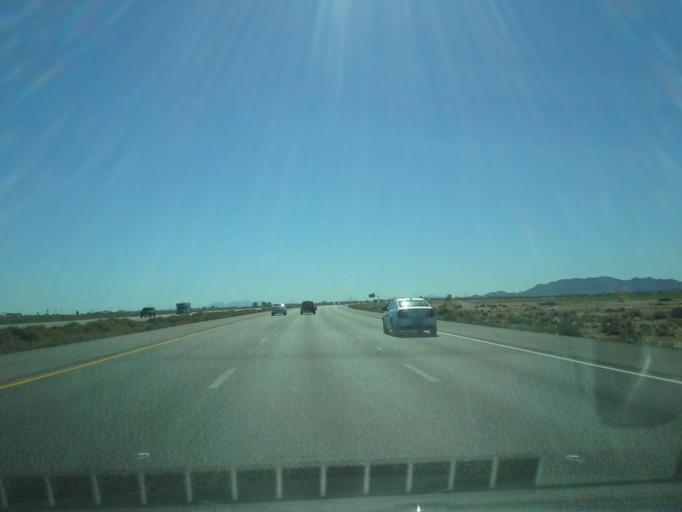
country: US
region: Arizona
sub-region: Pinal County
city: Casa Grande
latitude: 32.9181
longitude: -111.6879
